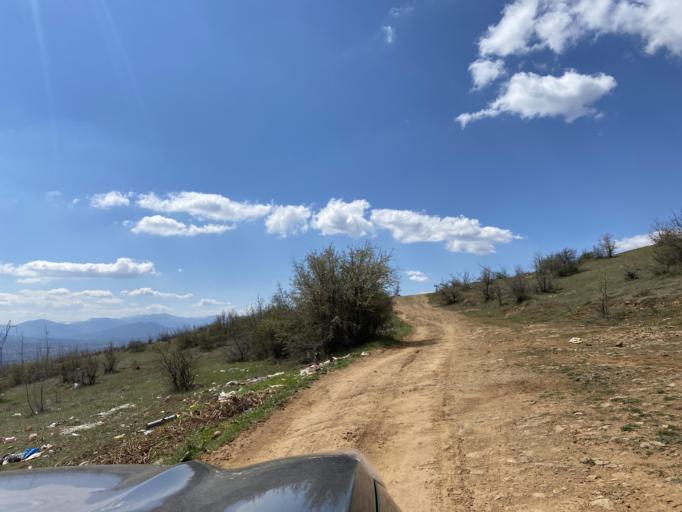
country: MK
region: Caska
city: Caska
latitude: 41.7296
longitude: 21.6641
